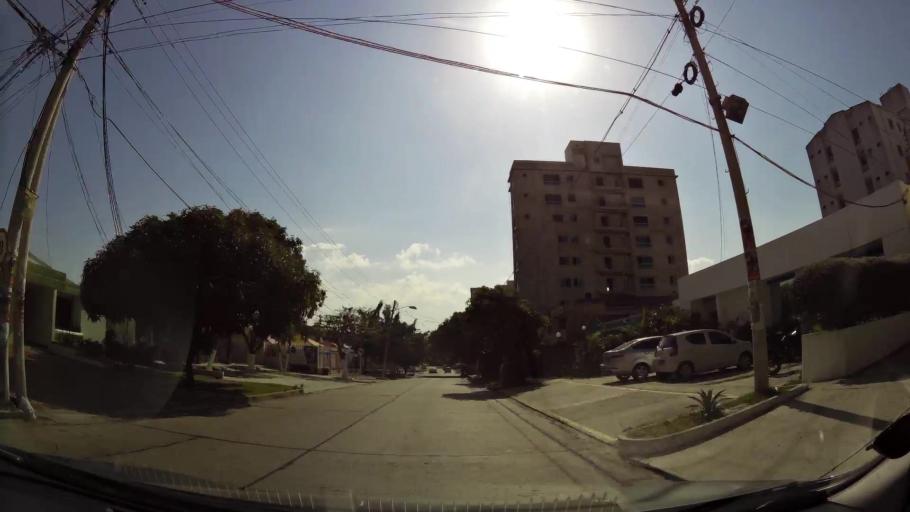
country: CO
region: Atlantico
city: Barranquilla
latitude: 11.0004
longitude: -74.8205
